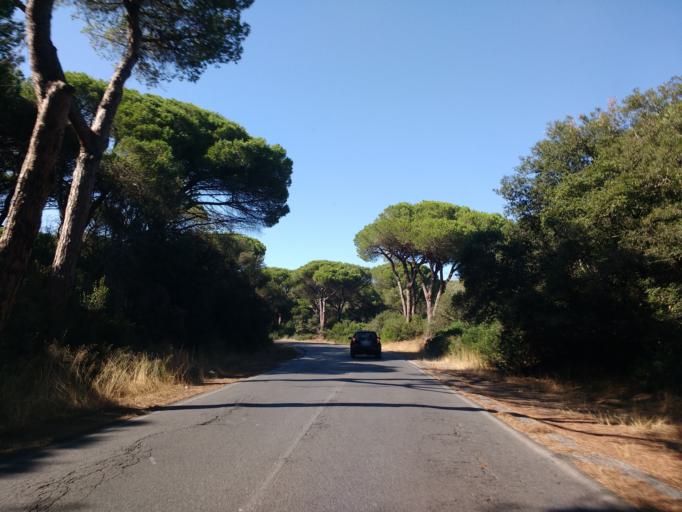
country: IT
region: Latium
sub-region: Citta metropolitana di Roma Capitale
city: Acilia-Castel Fusano-Ostia Antica
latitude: 41.7112
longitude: 12.3580
